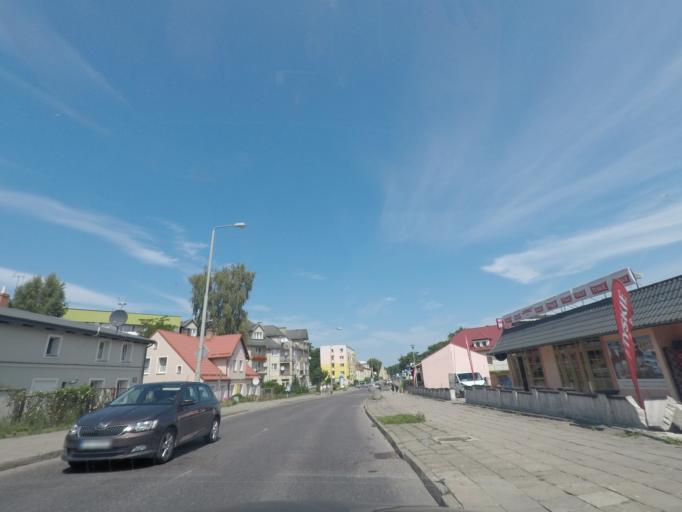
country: PL
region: Pomeranian Voivodeship
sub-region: Powiat slupski
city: Ustka
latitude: 54.5768
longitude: 16.8535
